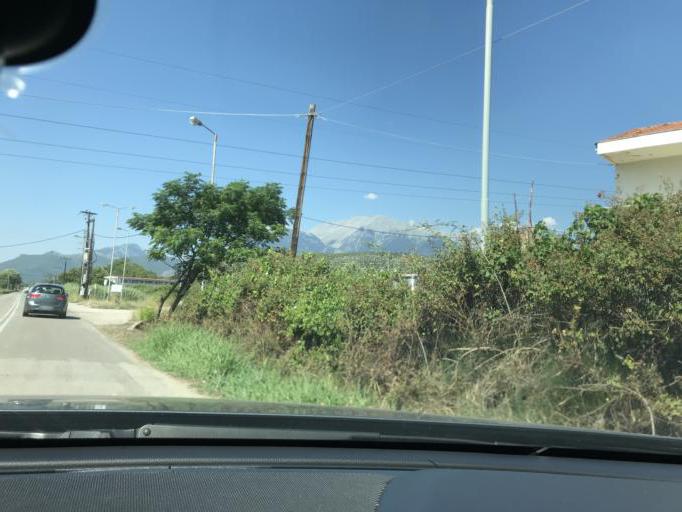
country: GR
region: Central Greece
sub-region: Nomos Fthiotidos
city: Elateia
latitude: 38.5350
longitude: 22.8101
